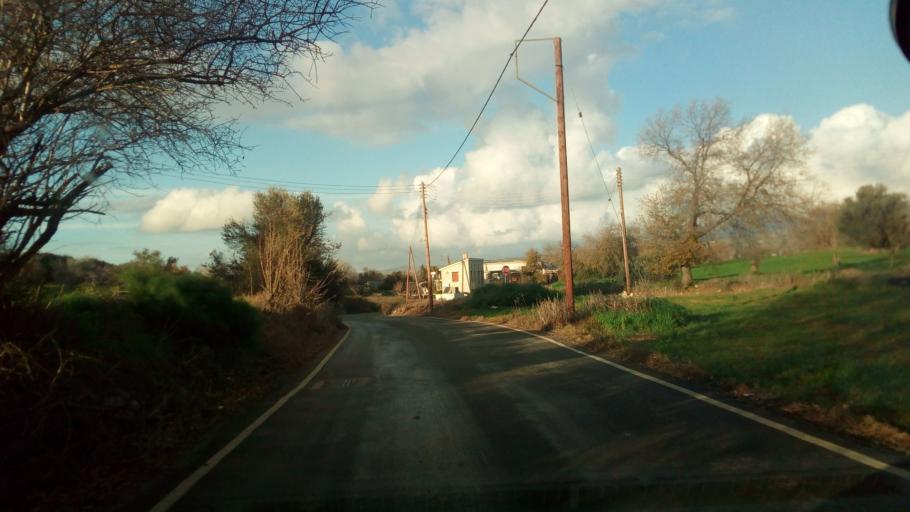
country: CY
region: Pafos
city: Mesogi
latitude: 34.8795
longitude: 32.5048
